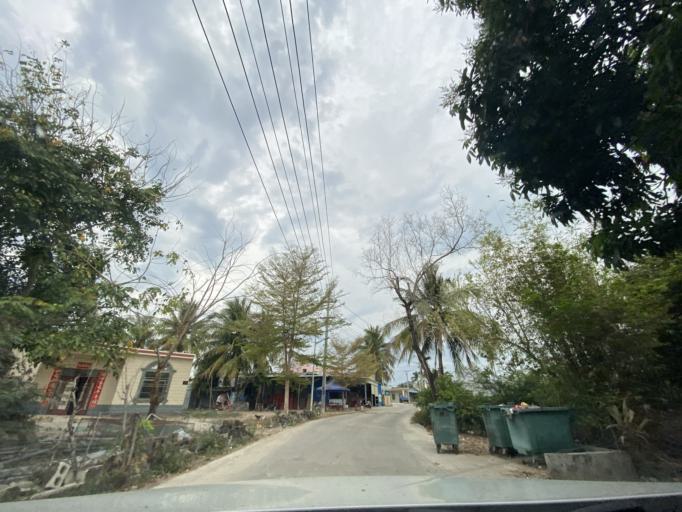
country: CN
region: Hainan
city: Yingzhou
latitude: 18.4164
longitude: 109.8228
